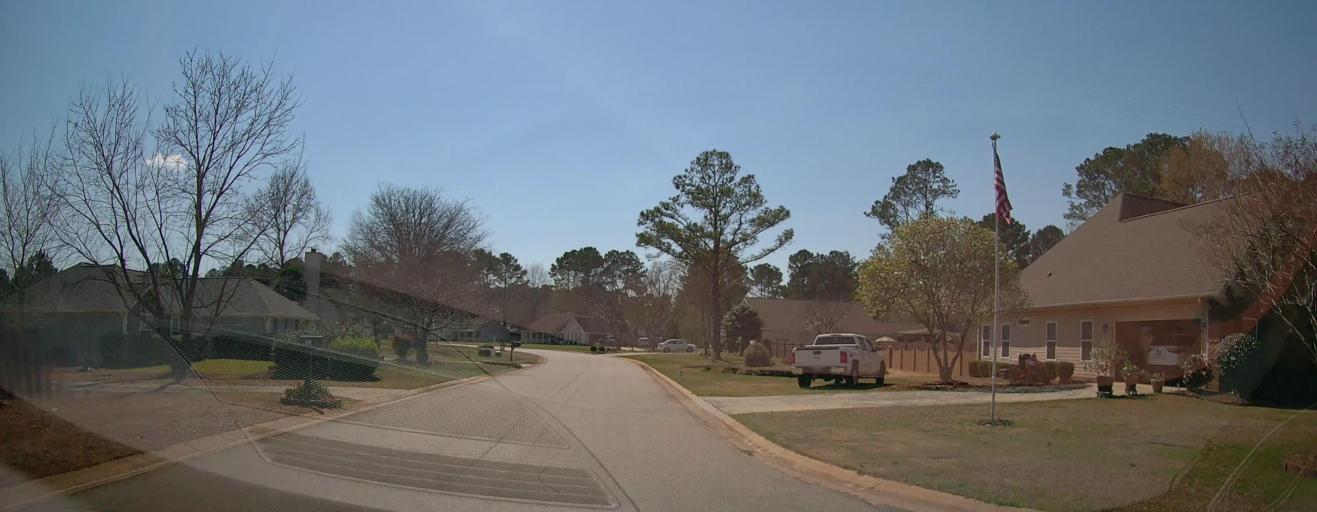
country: US
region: Georgia
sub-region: Houston County
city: Centerville
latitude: 32.5901
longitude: -83.7091
